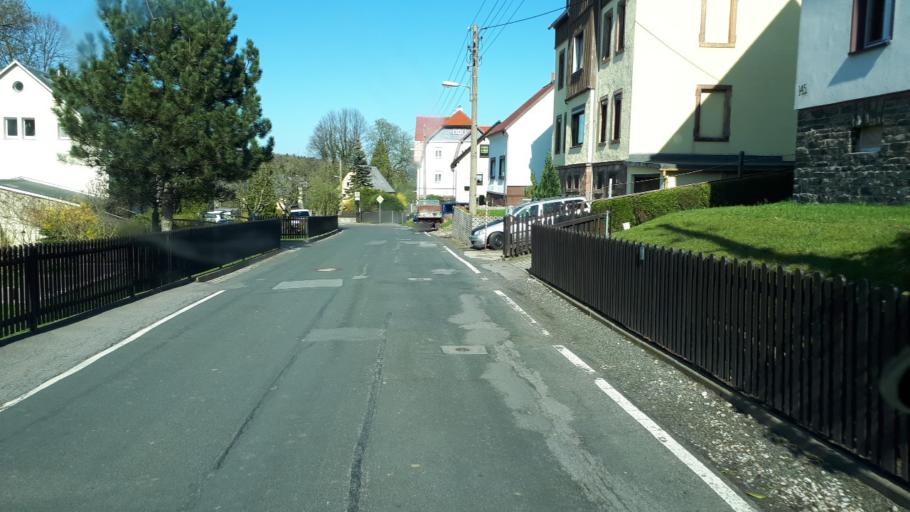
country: DE
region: Saxony
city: Burkhardtsdorf
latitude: 50.7625
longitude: 12.9412
